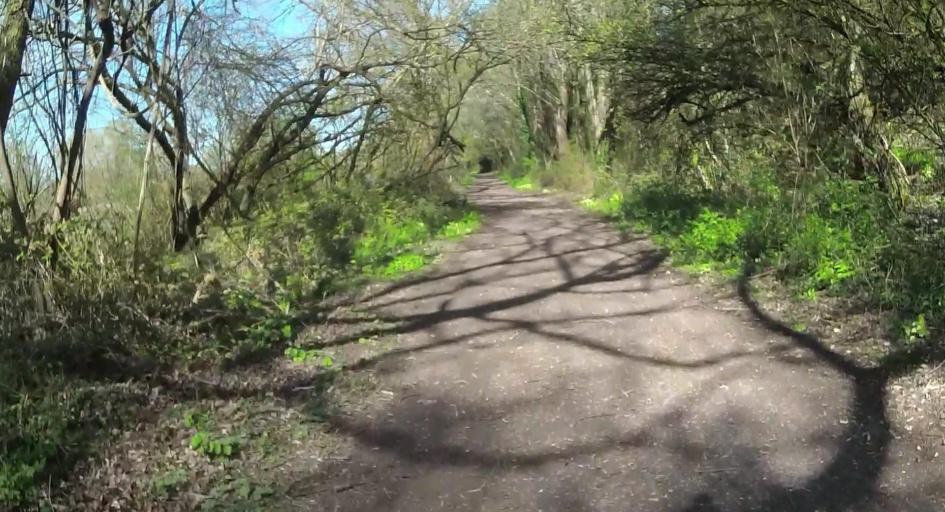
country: GB
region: England
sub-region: Hampshire
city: Romsey
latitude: 51.0785
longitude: -1.5035
